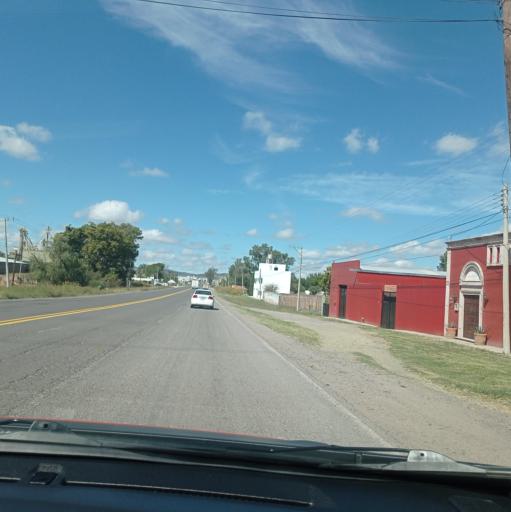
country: MX
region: Jalisco
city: San Miguel el Alto
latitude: 21.0267
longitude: -102.3766
